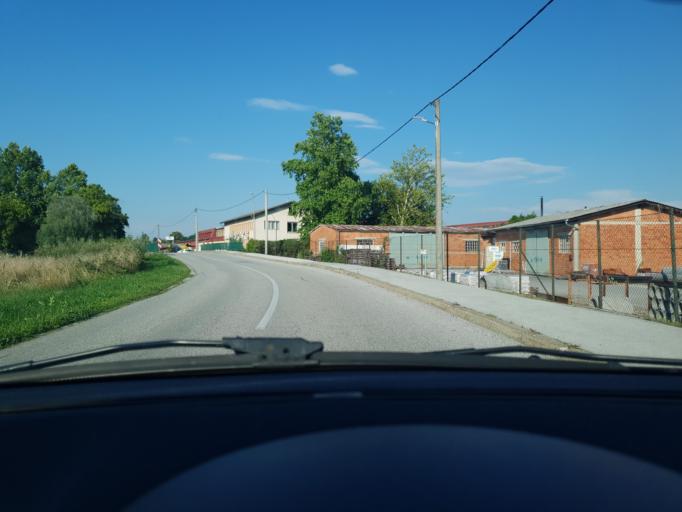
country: HR
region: Krapinsko-Zagorska
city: Oroslavje
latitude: 45.9989
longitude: 15.9245
